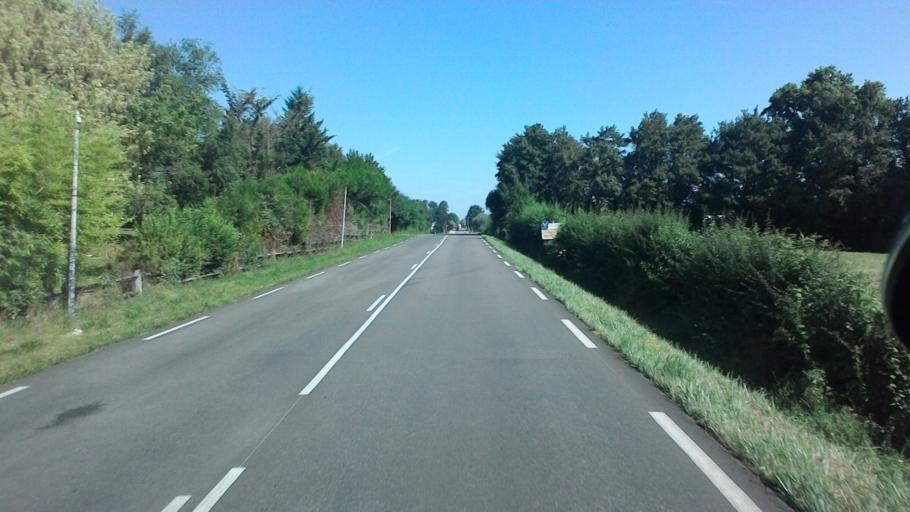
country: FR
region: Bourgogne
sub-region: Departement de Saone-et-Loire
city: Romenay
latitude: 46.4949
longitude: 5.0688
